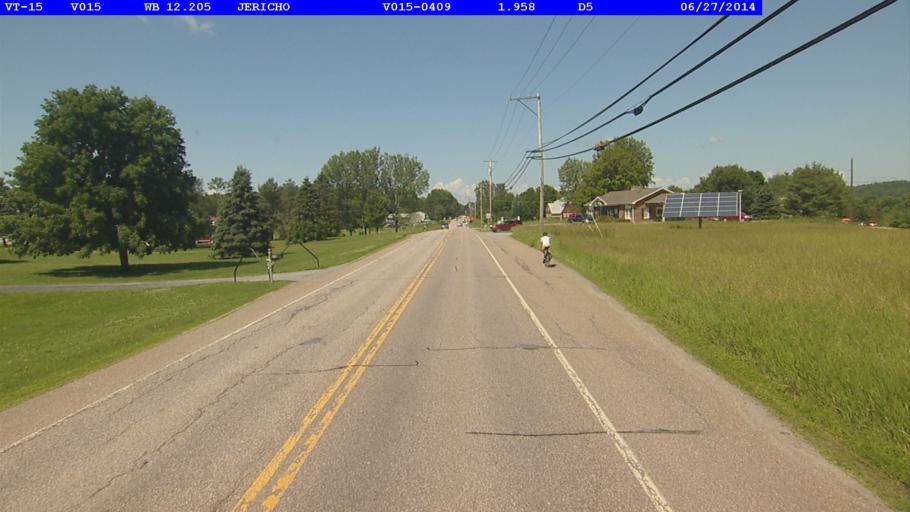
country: US
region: Vermont
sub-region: Chittenden County
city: Jericho
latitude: 44.5099
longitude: -72.9696
